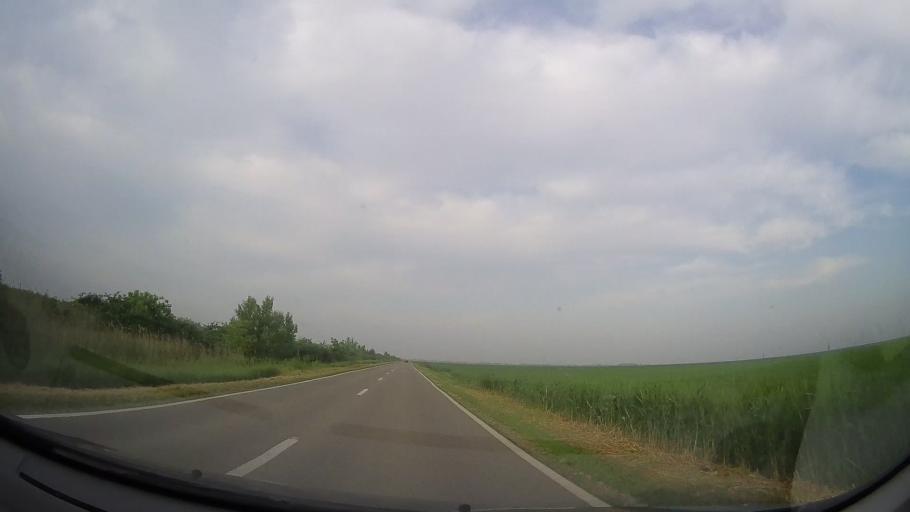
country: RO
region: Timis
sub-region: Comuna Peciu Nou
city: Peciu Nou
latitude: 45.6280
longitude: 21.0951
